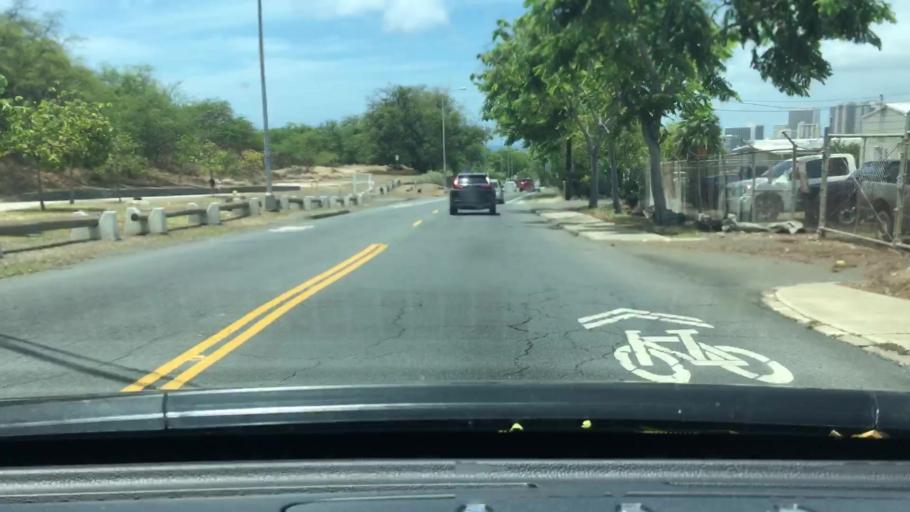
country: US
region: Hawaii
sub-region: Honolulu County
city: Honolulu
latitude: 21.2697
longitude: -157.8037
